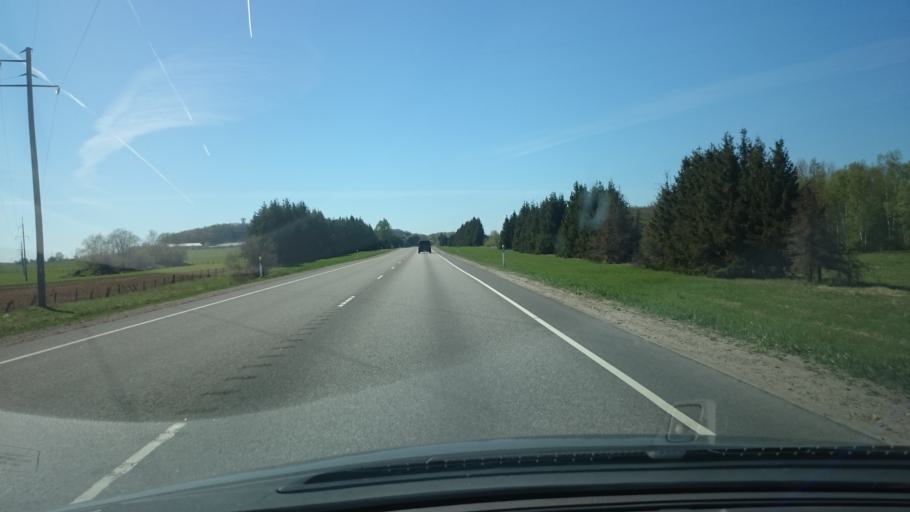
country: EE
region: Ida-Virumaa
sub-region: Sillamaee linn
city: Sillamae
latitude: 59.3770
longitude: 27.9053
